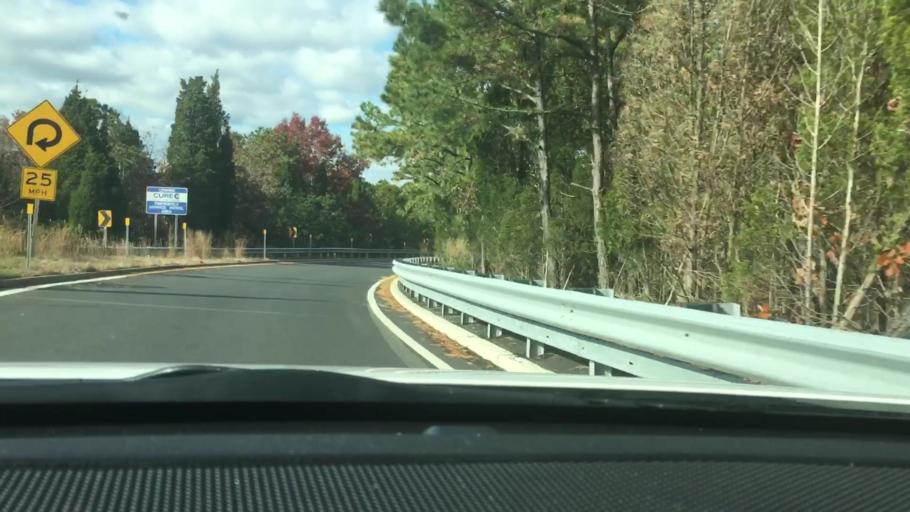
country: US
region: New Jersey
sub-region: Atlantic County
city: Pleasantville
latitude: 39.4145
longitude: -74.5544
